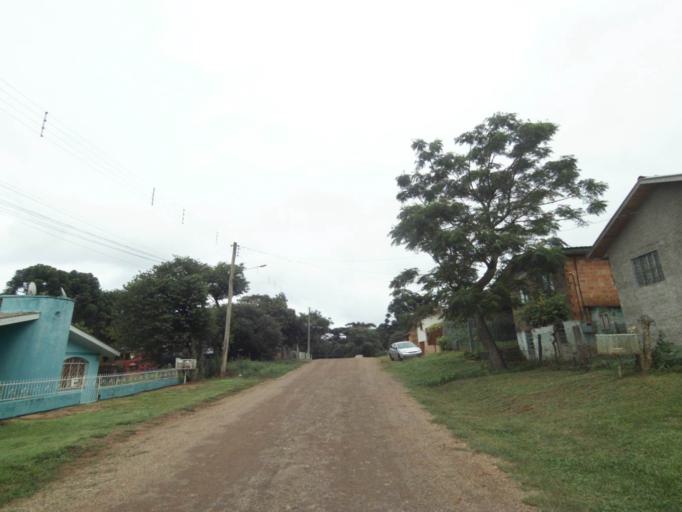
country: BR
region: Rio Grande do Sul
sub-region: Lagoa Vermelha
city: Lagoa Vermelha
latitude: -28.2190
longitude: -51.5231
